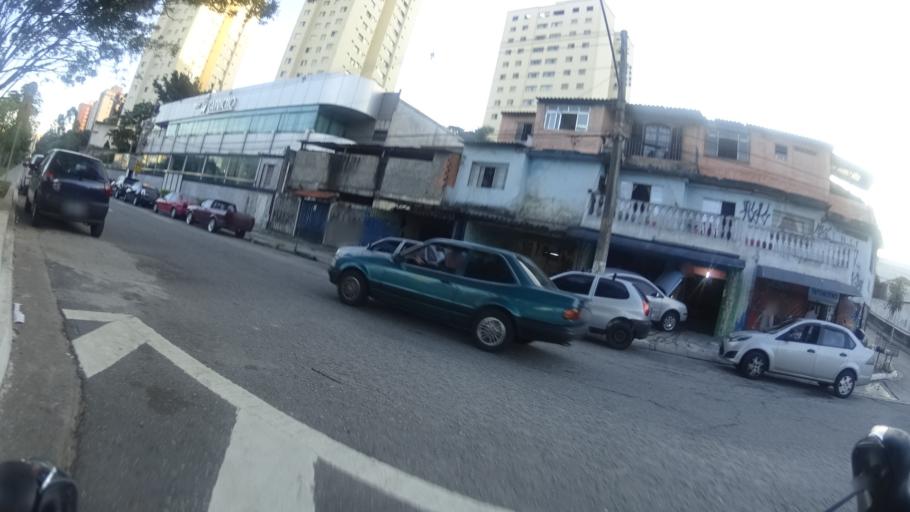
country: BR
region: Sao Paulo
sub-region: Sao Paulo
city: Sao Paulo
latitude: -23.4728
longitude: -46.6262
